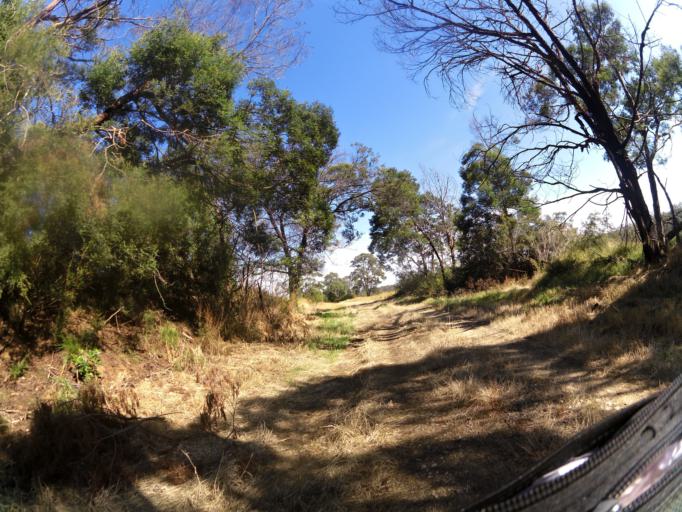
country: AU
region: Victoria
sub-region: East Gippsland
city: Lakes Entrance
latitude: -37.7387
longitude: 148.1686
